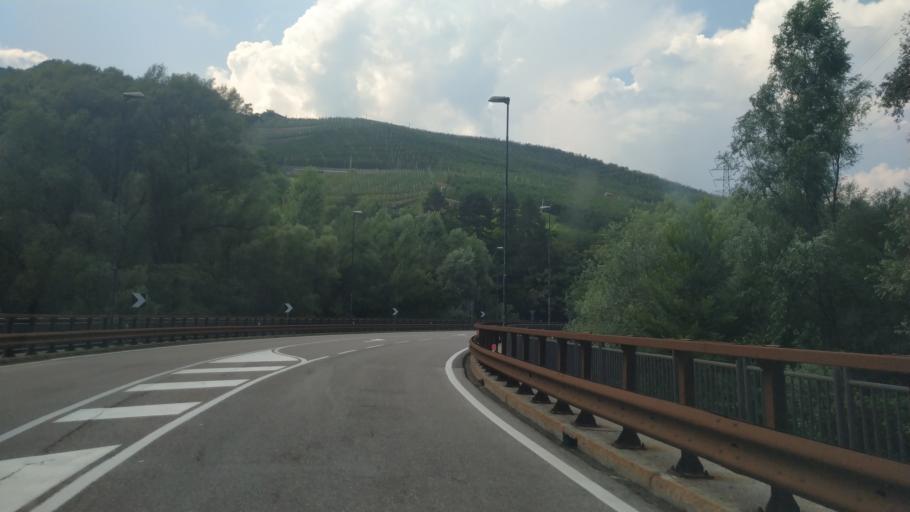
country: IT
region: Trentino-Alto Adige
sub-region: Provincia di Trento
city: Spormaggiore
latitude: 46.2376
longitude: 11.0566
